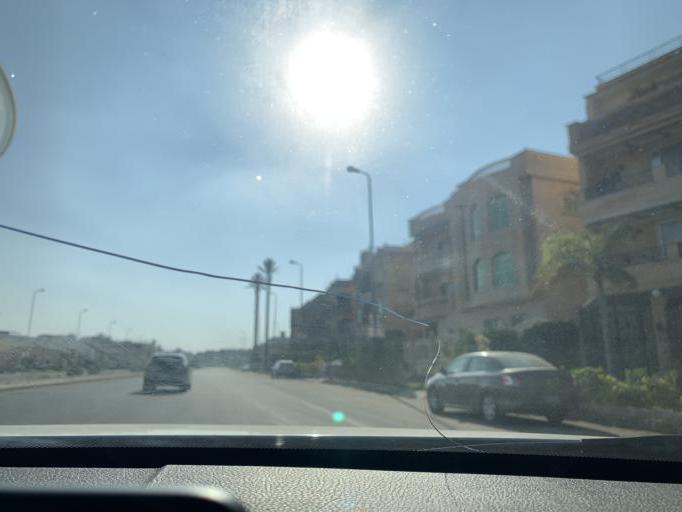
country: EG
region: Muhafazat al Qalyubiyah
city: Al Khankah
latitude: 30.0072
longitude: 31.4825
